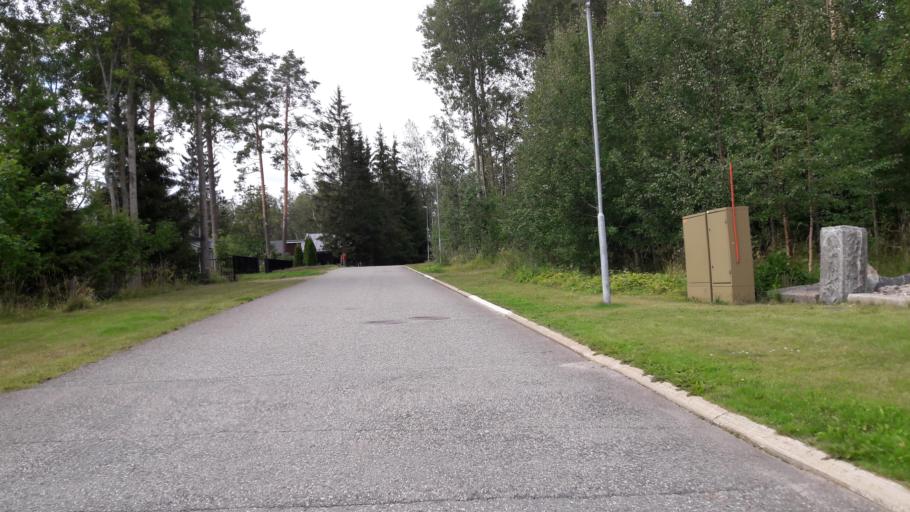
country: FI
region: North Karelia
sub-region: Joensuu
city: Joensuu
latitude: 62.5750
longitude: 29.7783
